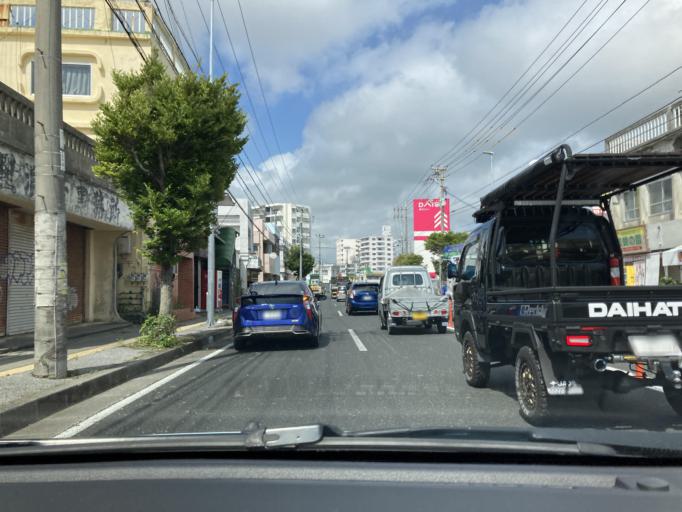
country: JP
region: Okinawa
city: Okinawa
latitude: 26.3340
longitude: 127.8192
